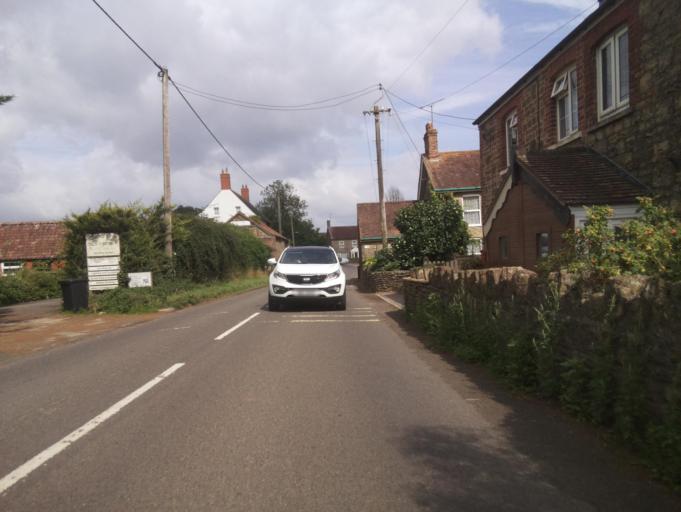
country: GB
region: England
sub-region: Somerset
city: Wincanton
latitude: 51.0057
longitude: -2.4198
